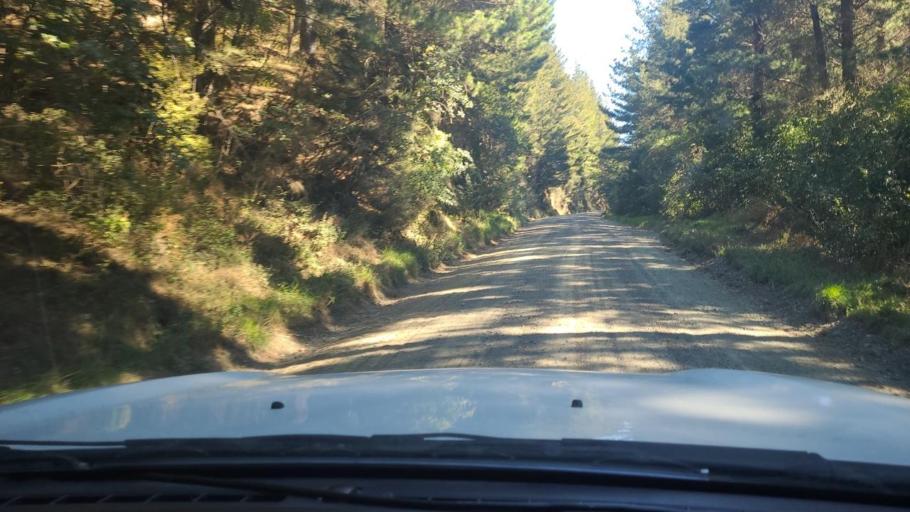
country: NZ
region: Hawke's Bay
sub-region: Napier City
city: Taradale
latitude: -39.4080
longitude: 176.4762
